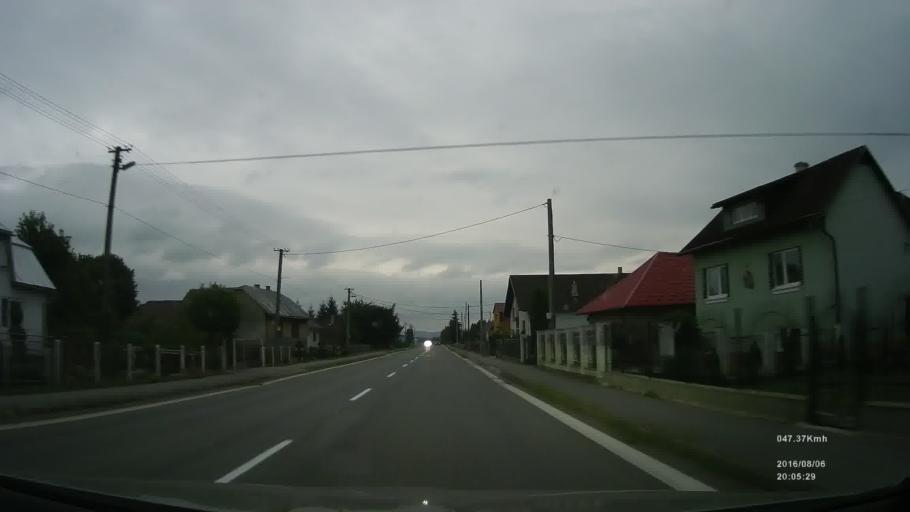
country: SK
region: Presovsky
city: Stropkov
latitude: 49.2346
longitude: 21.6262
